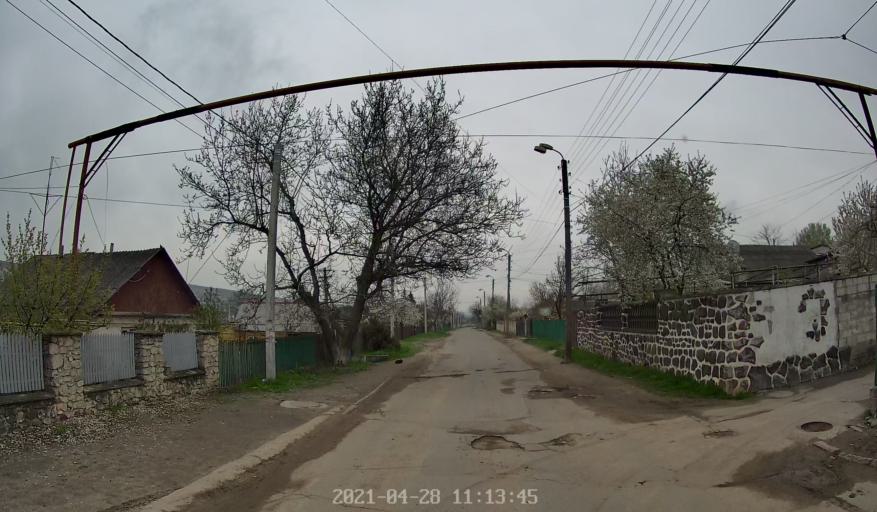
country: MD
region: Chisinau
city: Singera
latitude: 46.9832
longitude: 28.9366
